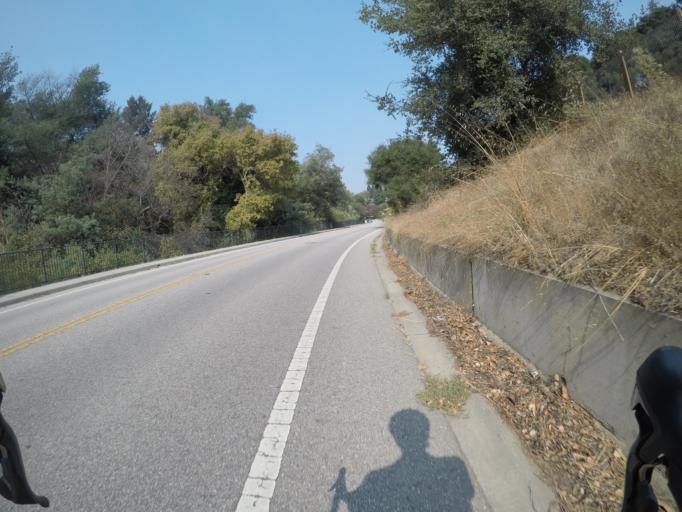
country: US
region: California
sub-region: Santa Cruz County
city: Scotts Valley
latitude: 37.0395
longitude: -122.0222
